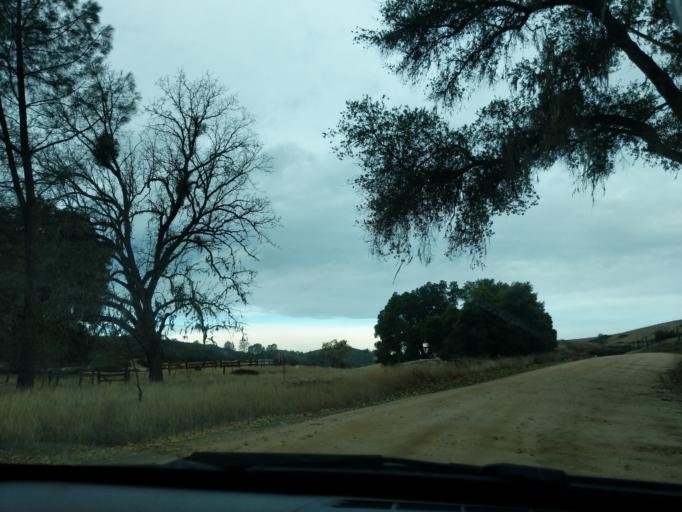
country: US
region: California
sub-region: Monterey County
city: Soledad
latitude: 36.5518
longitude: -121.2619
